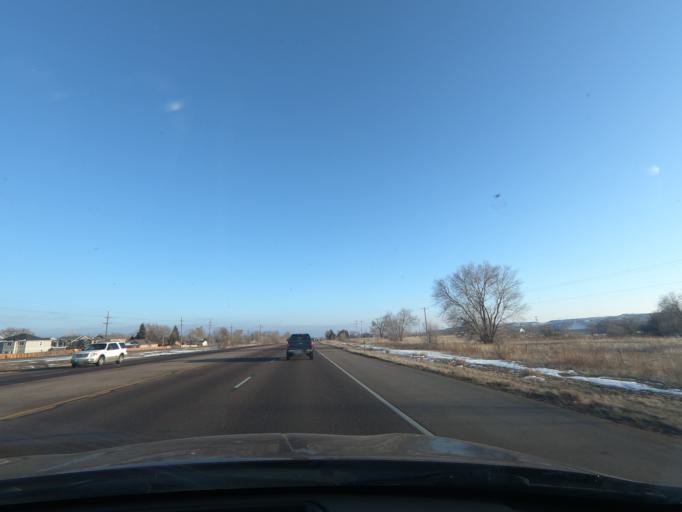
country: US
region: Colorado
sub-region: El Paso County
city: Stratmoor
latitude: 38.7622
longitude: -104.7546
